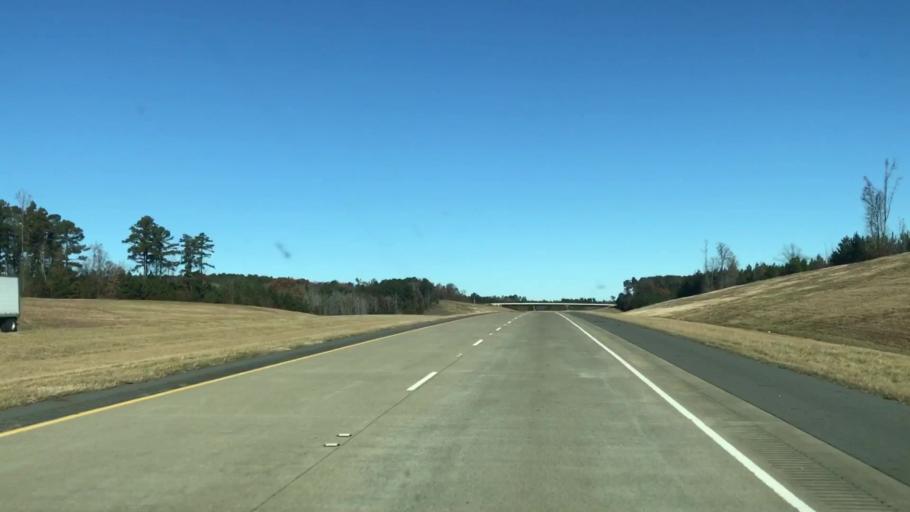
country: US
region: Louisiana
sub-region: Caddo Parish
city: Vivian
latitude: 32.9693
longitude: -93.9063
